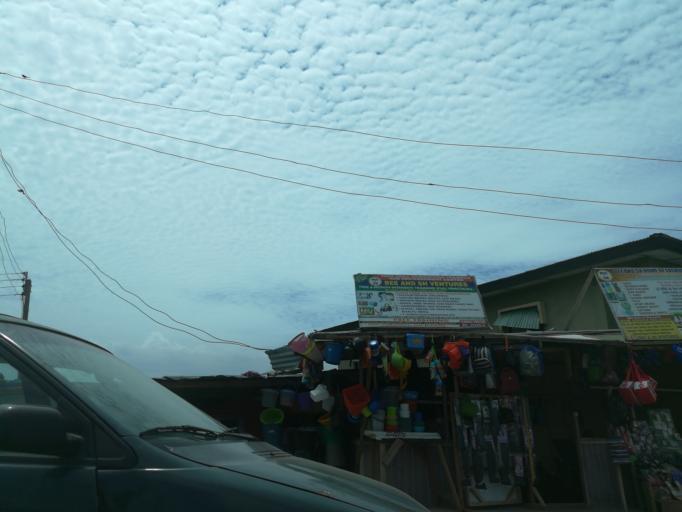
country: NG
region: Lagos
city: Ebute Ikorodu
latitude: 6.5542
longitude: 3.4754
